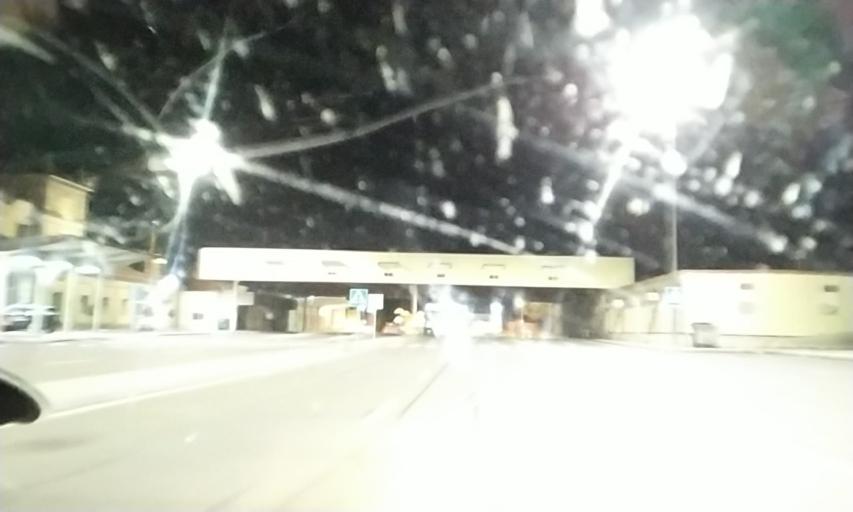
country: ES
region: Castille and Leon
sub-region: Provincia de Salamanca
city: Fuentes de Onoro
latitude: 40.6062
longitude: -6.8248
